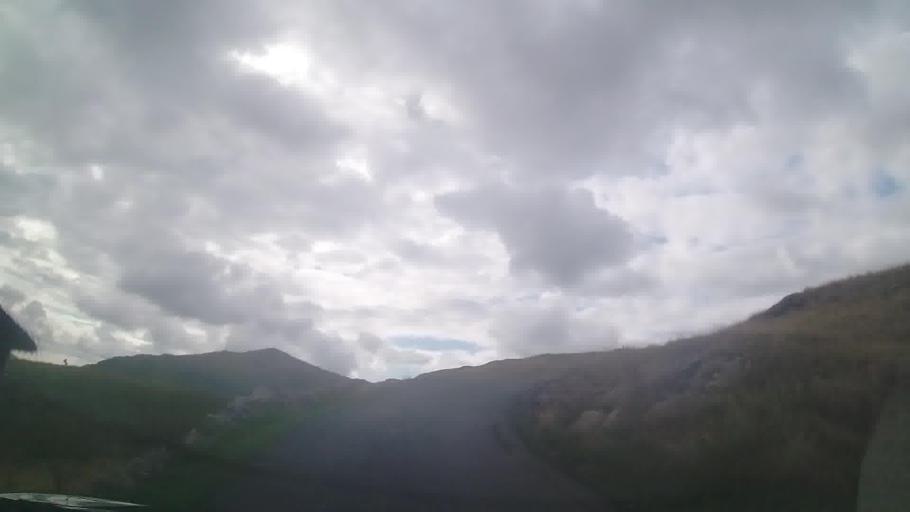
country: GB
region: England
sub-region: Cumbria
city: Keswick
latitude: 54.4028
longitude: -3.1838
